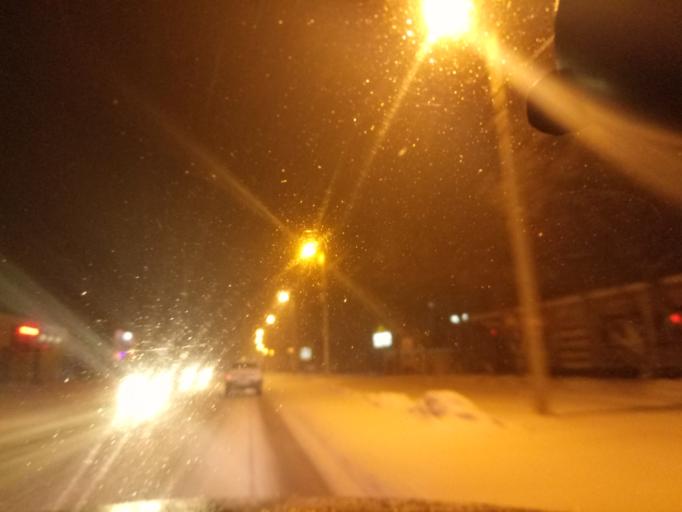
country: RU
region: Tula
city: Novomoskovsk
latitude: 53.9920
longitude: 38.2972
